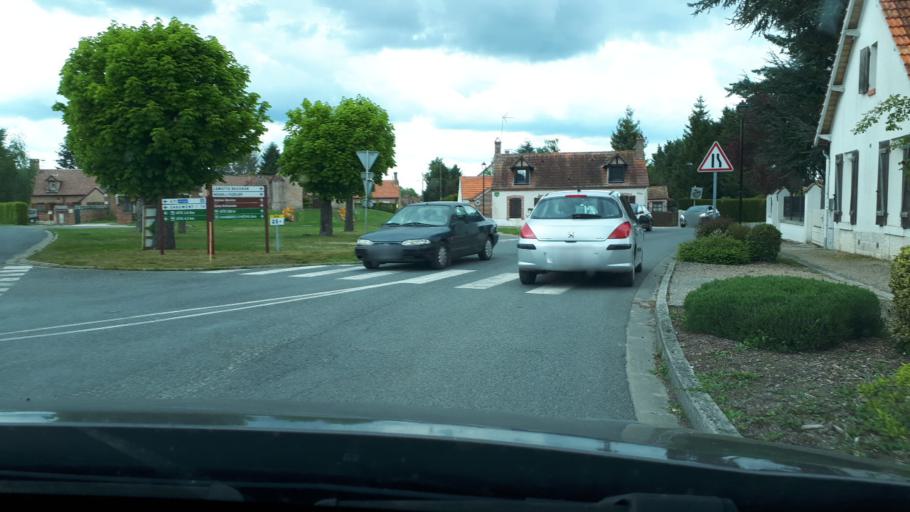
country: FR
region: Centre
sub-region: Departement du Loir-et-Cher
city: Saint-Viatre
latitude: 47.5250
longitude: 1.9336
